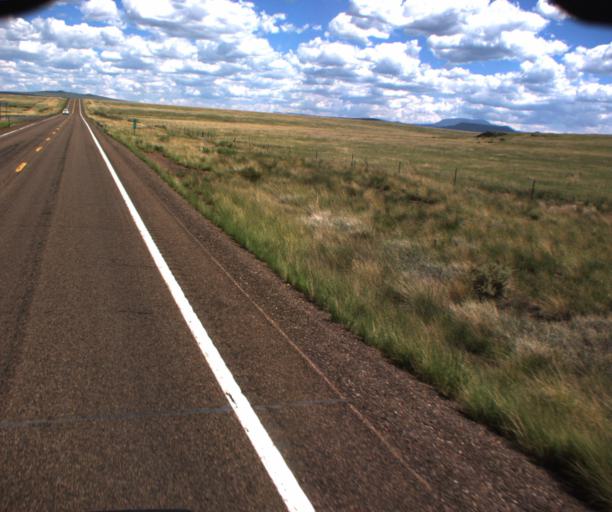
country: US
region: Arizona
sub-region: Apache County
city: Springerville
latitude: 34.1946
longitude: -109.3723
